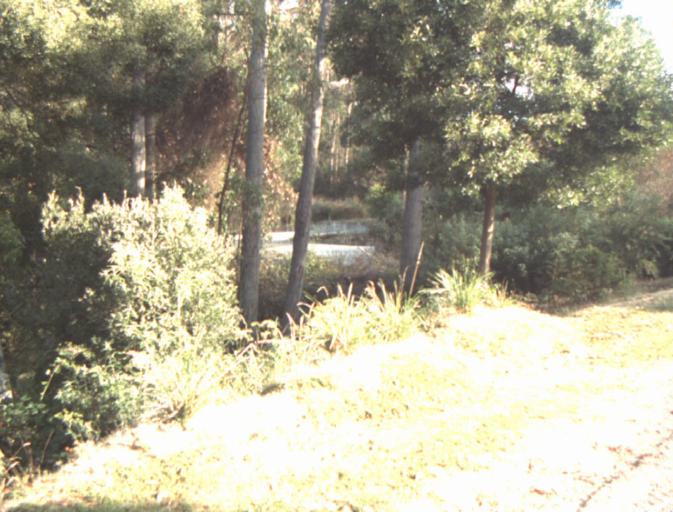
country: AU
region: Tasmania
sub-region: Launceston
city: Mayfield
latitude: -41.2173
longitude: 147.2089
